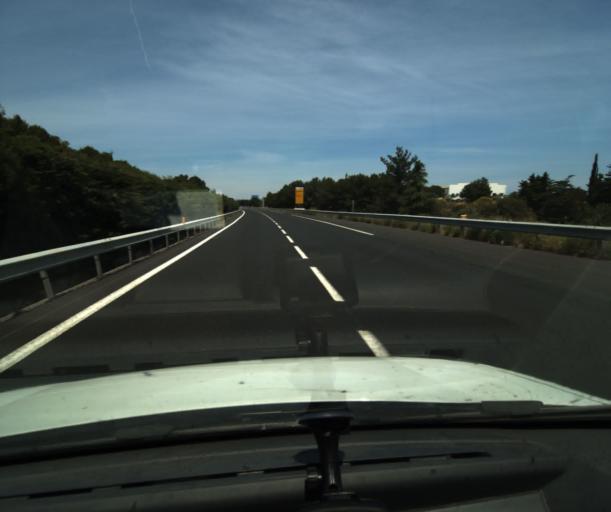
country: FR
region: Languedoc-Roussillon
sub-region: Departement des Pyrenees-Orientales
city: Pia
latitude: 42.7481
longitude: 2.8922
